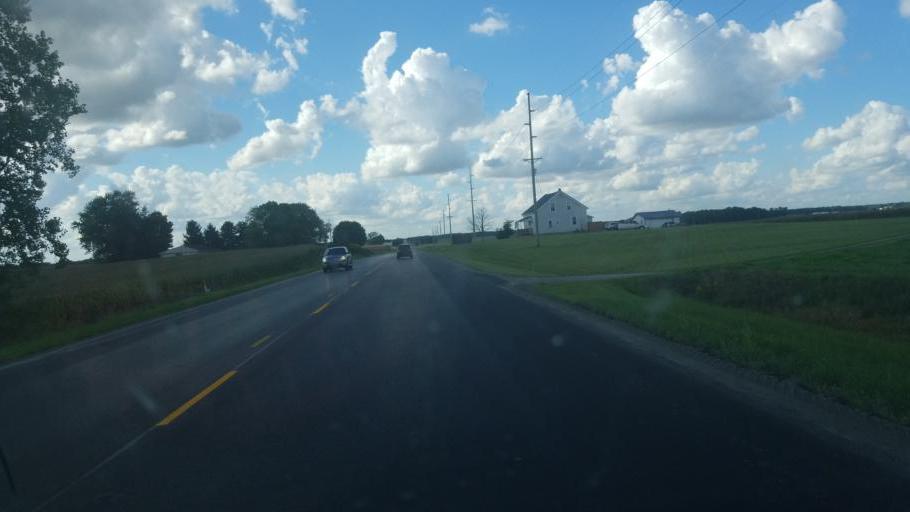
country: US
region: Ohio
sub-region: Hardin County
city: Kenton
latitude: 40.6620
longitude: -83.6473
